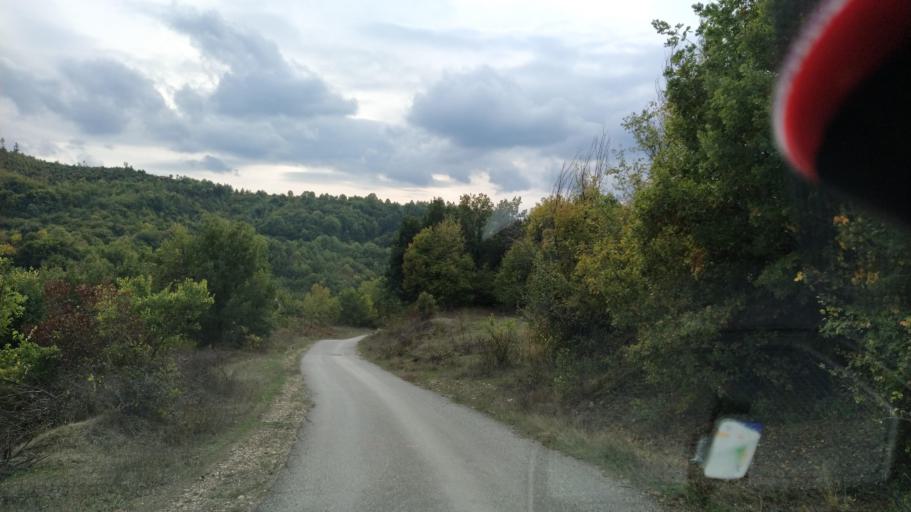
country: MK
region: Strumica
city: Veljusa
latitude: 41.5118
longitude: 22.4893
